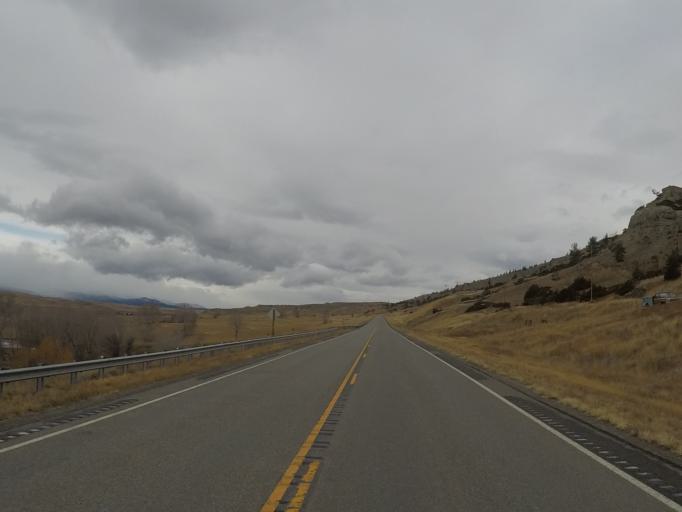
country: US
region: Montana
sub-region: Sweet Grass County
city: Big Timber
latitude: 45.8868
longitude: -109.9583
